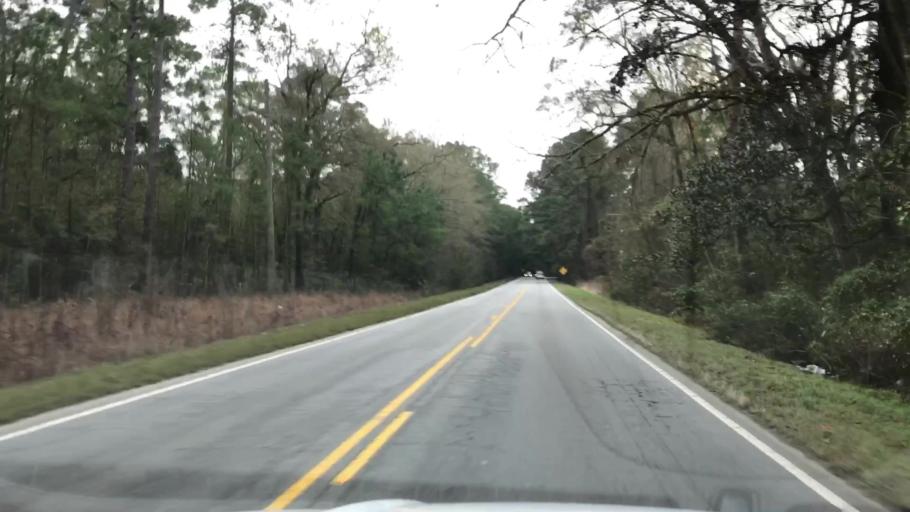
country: US
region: South Carolina
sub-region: Jasper County
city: Ridgeland
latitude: 32.3906
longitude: -80.9076
